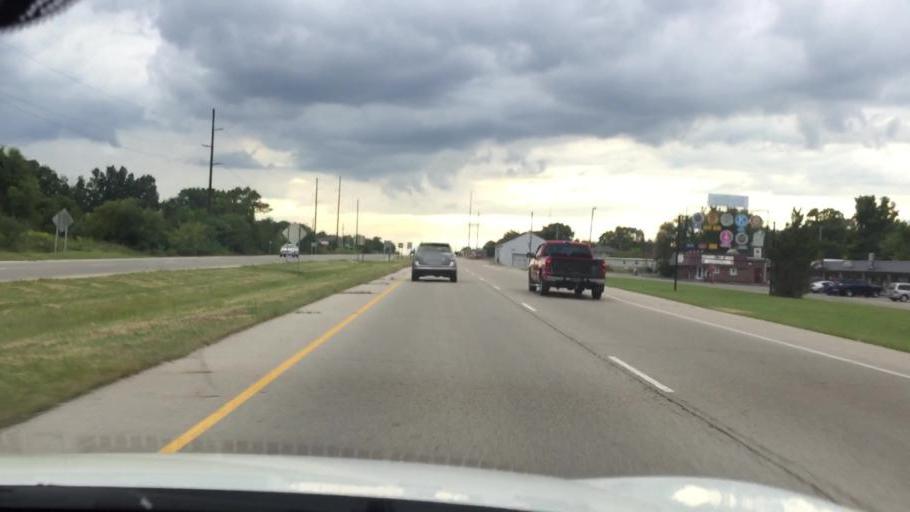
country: US
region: Ohio
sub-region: Clark County
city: Springfield
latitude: 39.9233
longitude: -83.7407
